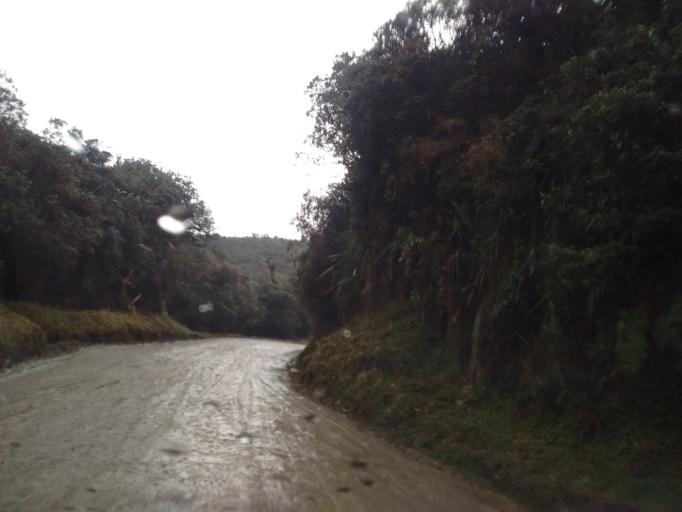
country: CO
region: Cauca
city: Paispamba
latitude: 2.1632
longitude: -76.3994
